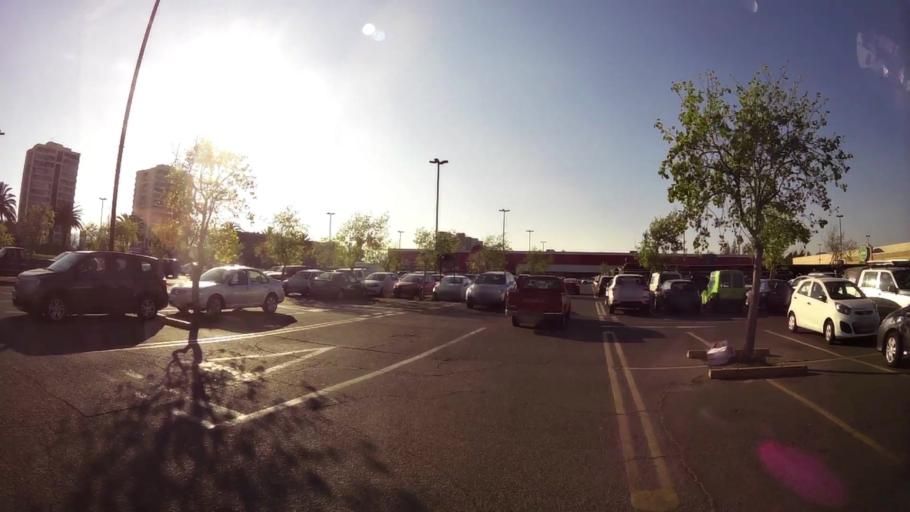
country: CL
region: Santiago Metropolitan
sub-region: Provincia de Santiago
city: Lo Prado
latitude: -33.4814
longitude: -70.7529
